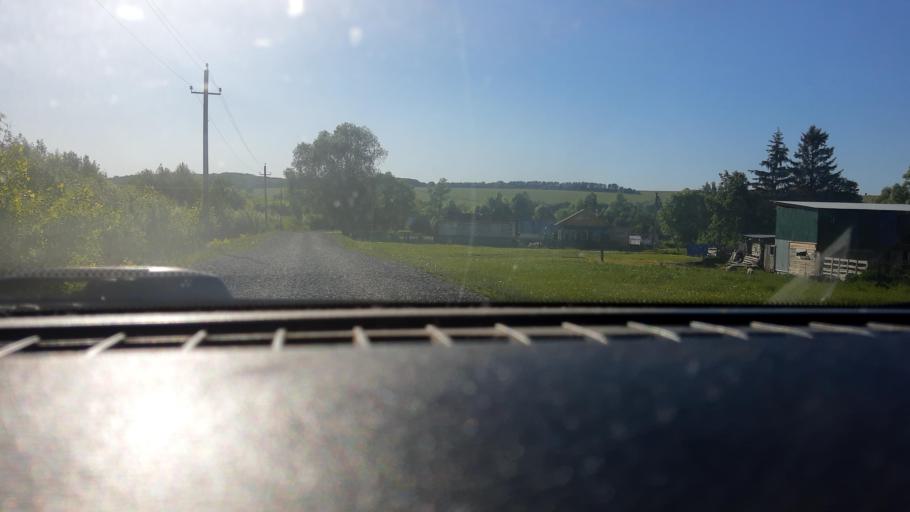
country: RU
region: Bashkortostan
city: Ulukulevo
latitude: 54.5595
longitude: 56.3318
